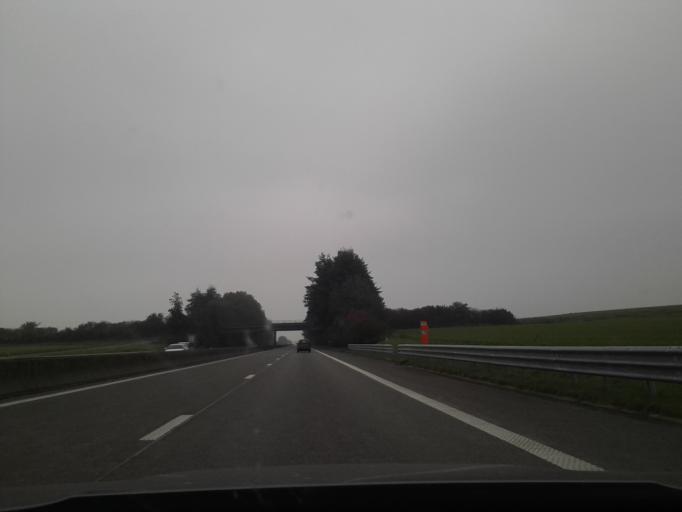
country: BE
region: Wallonia
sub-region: Province du Hainaut
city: Silly
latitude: 50.6885
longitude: 3.9552
